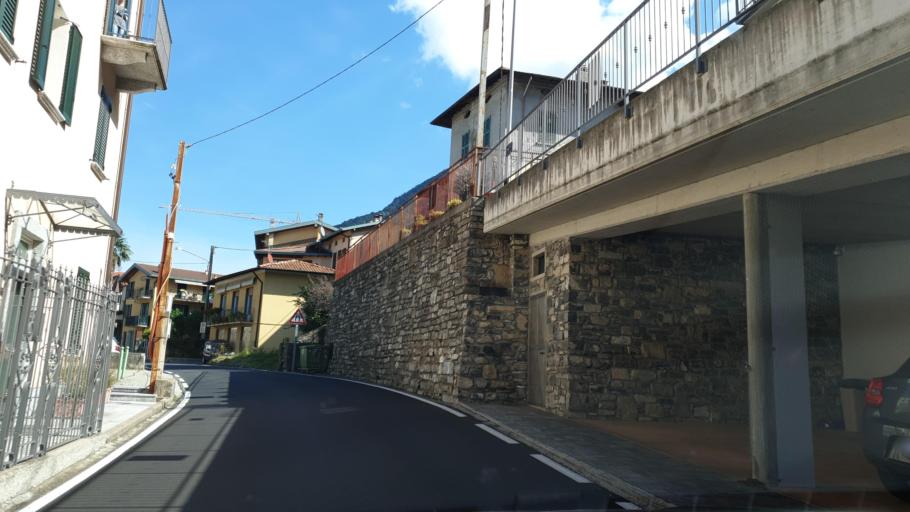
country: IT
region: Lombardy
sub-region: Provincia di Como
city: Lezzeno
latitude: 45.9469
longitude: 9.2024
